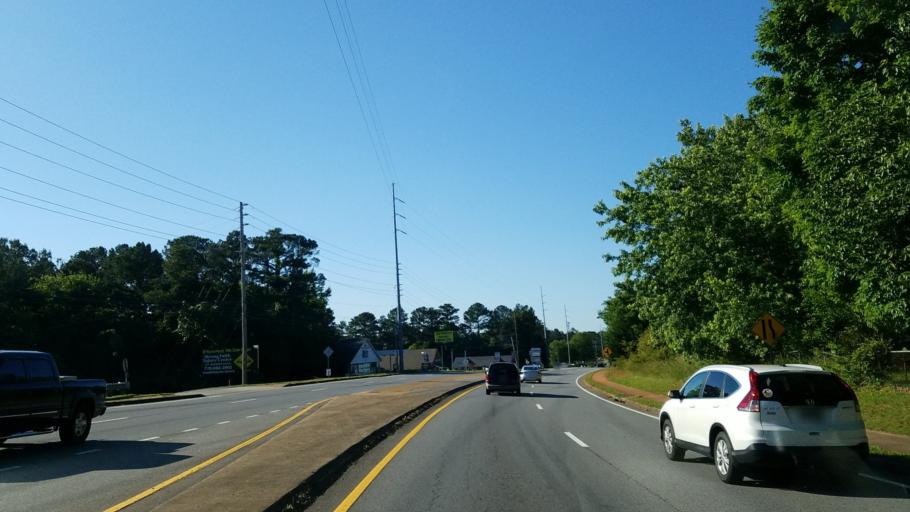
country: US
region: Georgia
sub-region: Cherokee County
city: Woodstock
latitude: 34.1203
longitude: -84.5858
